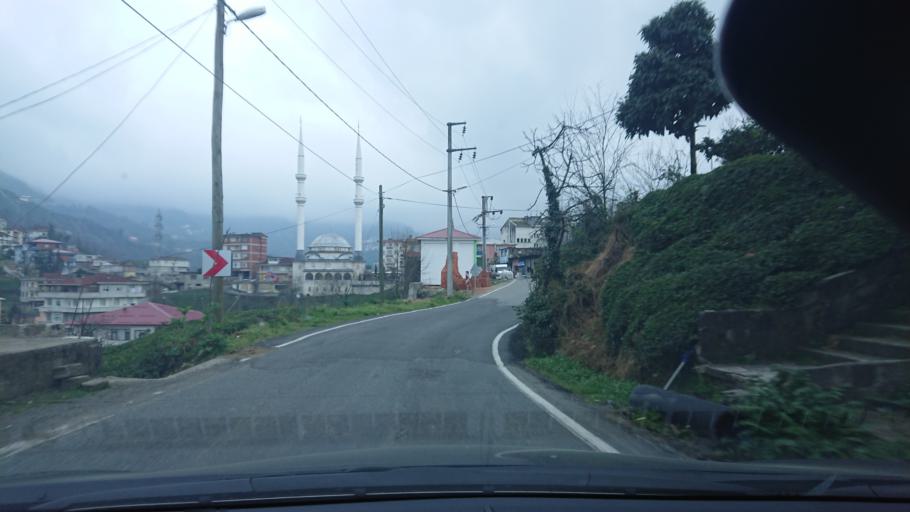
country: TR
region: Rize
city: Rize
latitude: 41.0007
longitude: 40.4879
